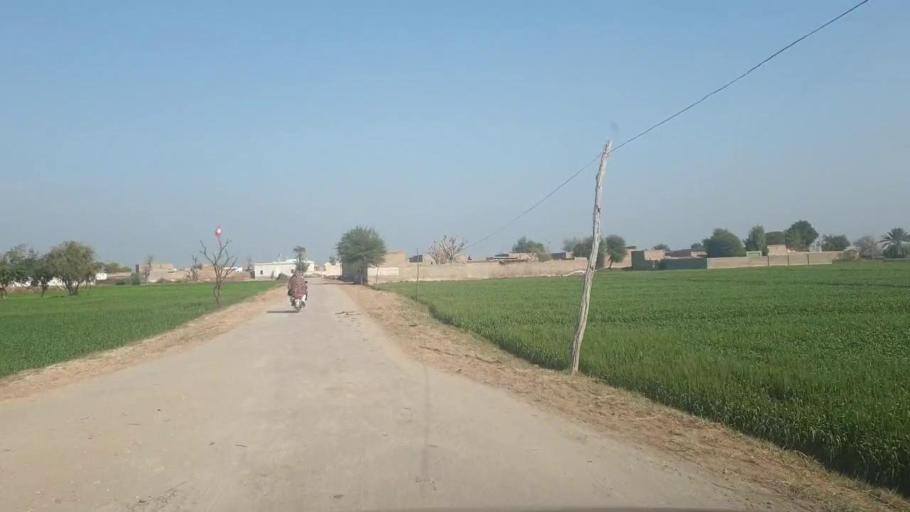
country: PK
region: Sindh
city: Sakrand
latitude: 26.0550
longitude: 68.4158
